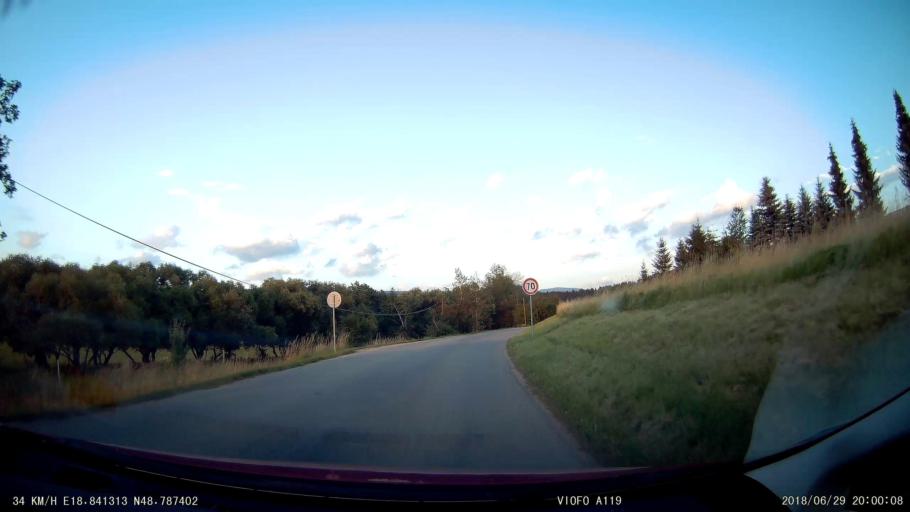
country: SK
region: Nitriansky
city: Handlova
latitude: 48.7874
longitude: 18.8414
